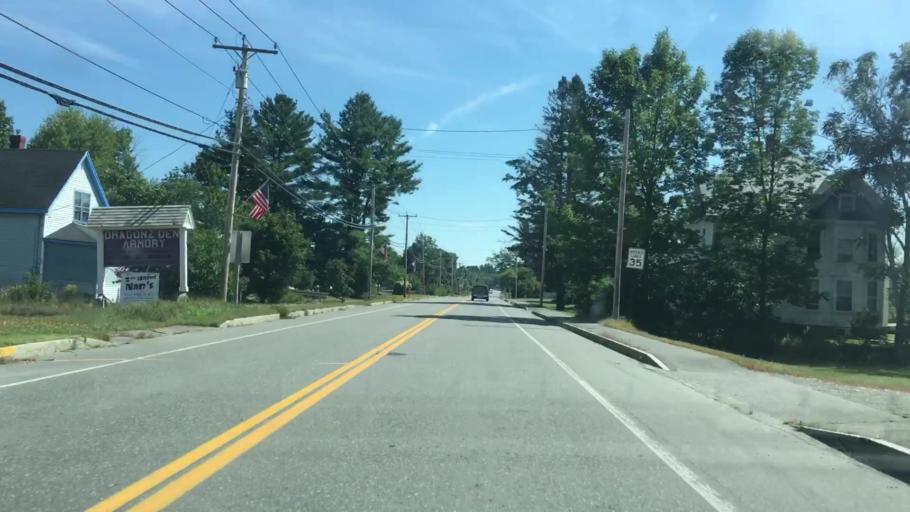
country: US
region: Maine
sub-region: Piscataquis County
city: Milo
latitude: 45.2484
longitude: -68.9797
